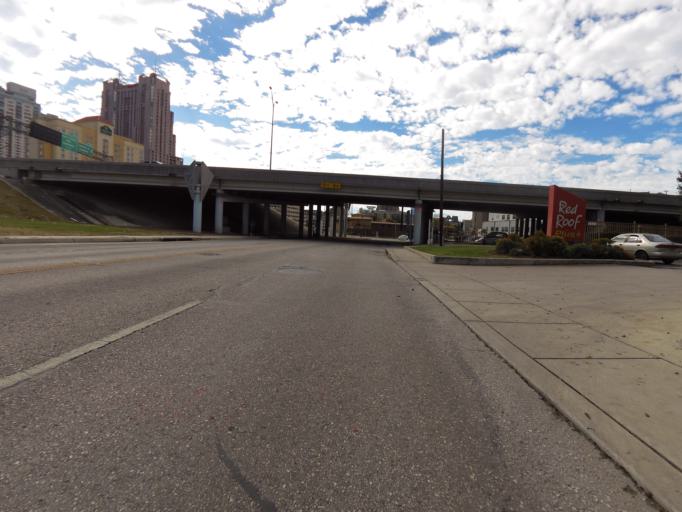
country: US
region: Texas
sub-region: Bexar County
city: San Antonio
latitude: 29.4252
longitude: -98.4809
